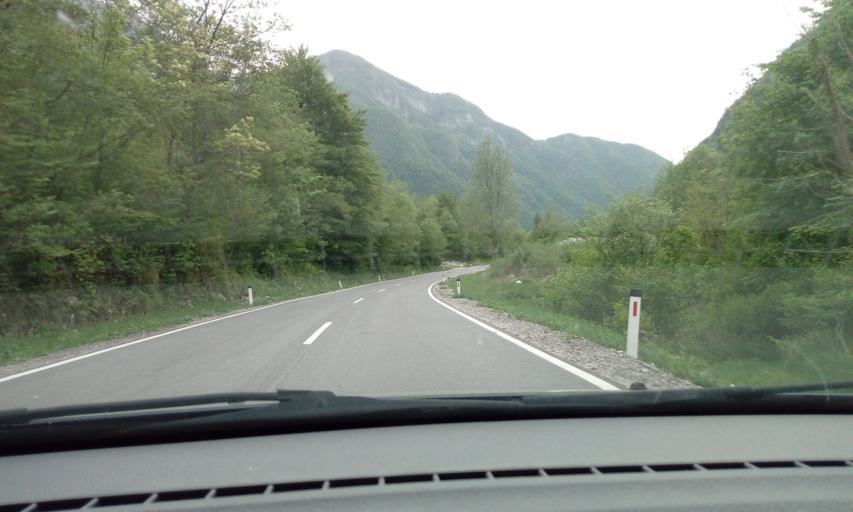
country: IT
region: Friuli Venezia Giulia
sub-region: Provincia di Udine
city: Pulfero
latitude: 46.2292
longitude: 13.5011
